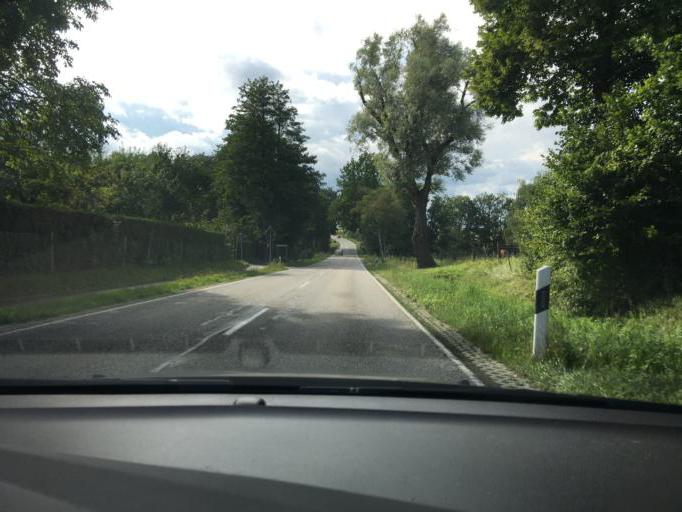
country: DE
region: Bavaria
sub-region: Upper Bavaria
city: Bockhorn
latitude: 48.2948
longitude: 11.9545
